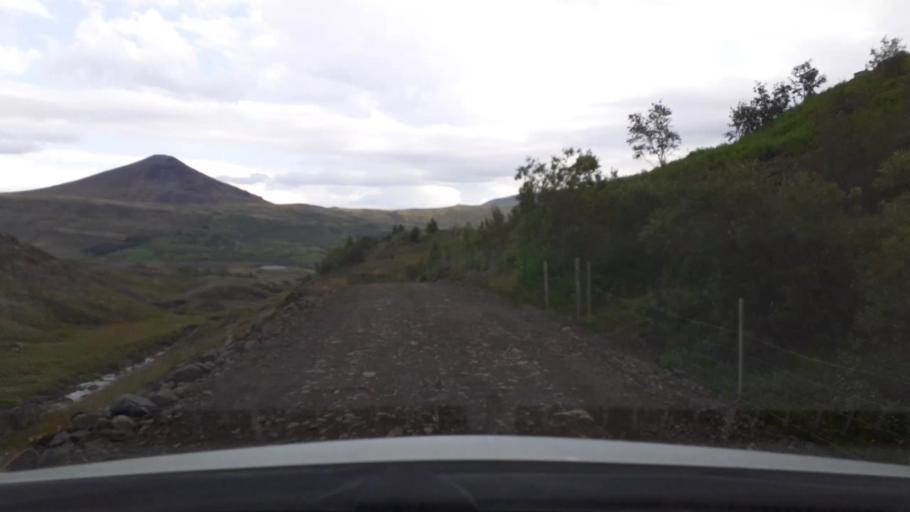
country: IS
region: Capital Region
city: Mosfellsbaer
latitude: 64.2845
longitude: -21.4630
